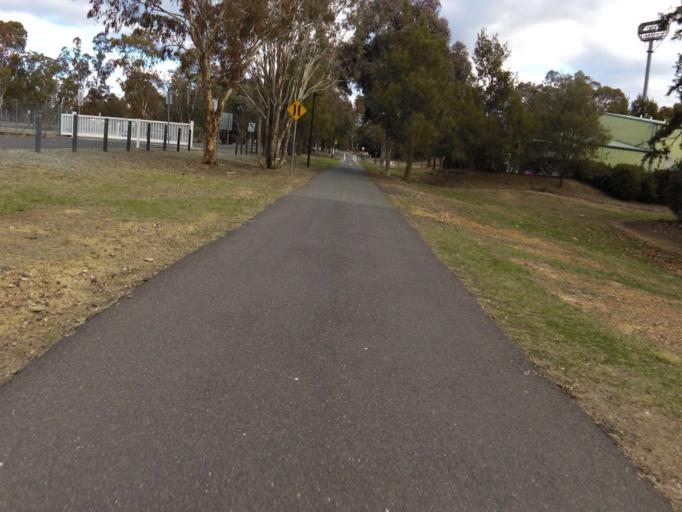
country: AU
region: Australian Capital Territory
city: Kaleen
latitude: -35.2485
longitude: 149.1052
